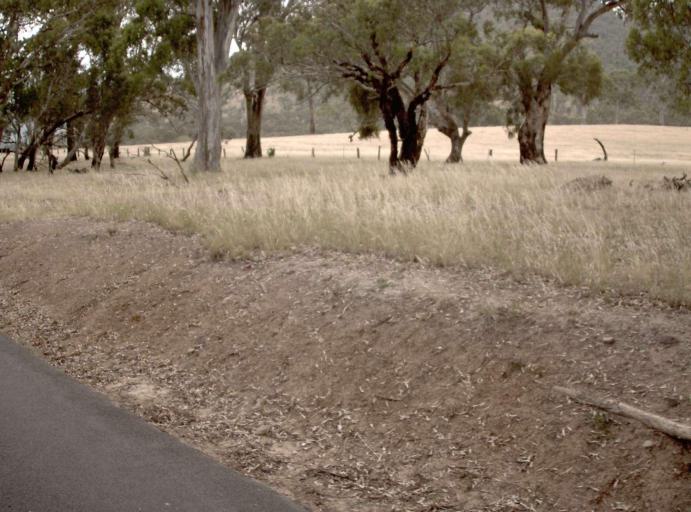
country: AU
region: Victoria
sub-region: Wellington
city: Heyfield
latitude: -37.6526
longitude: 146.6425
